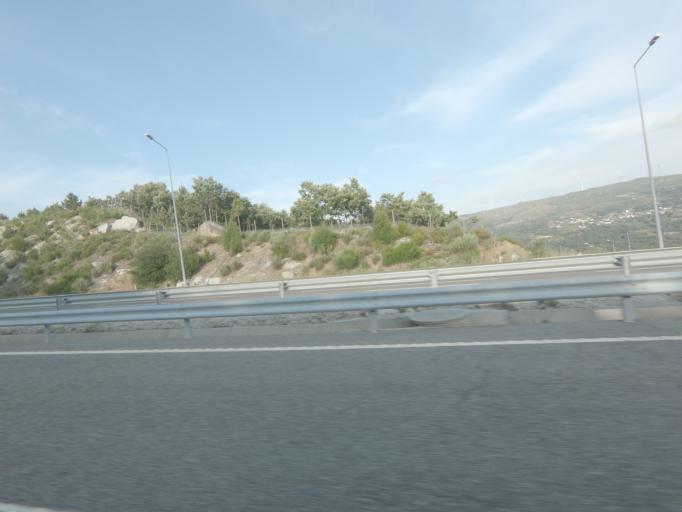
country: PT
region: Vila Real
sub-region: Vila Pouca de Aguiar
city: Vila Pouca de Aguiar
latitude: 41.4912
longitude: -7.6604
